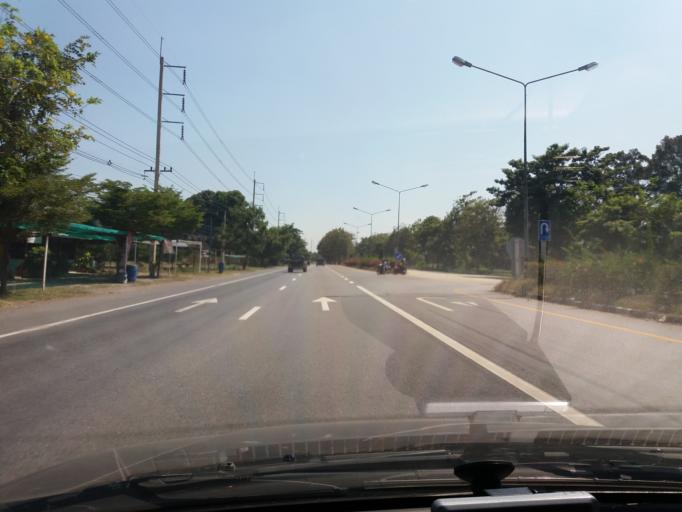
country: TH
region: Chai Nat
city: Chai Nat
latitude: 15.1262
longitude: 100.1480
